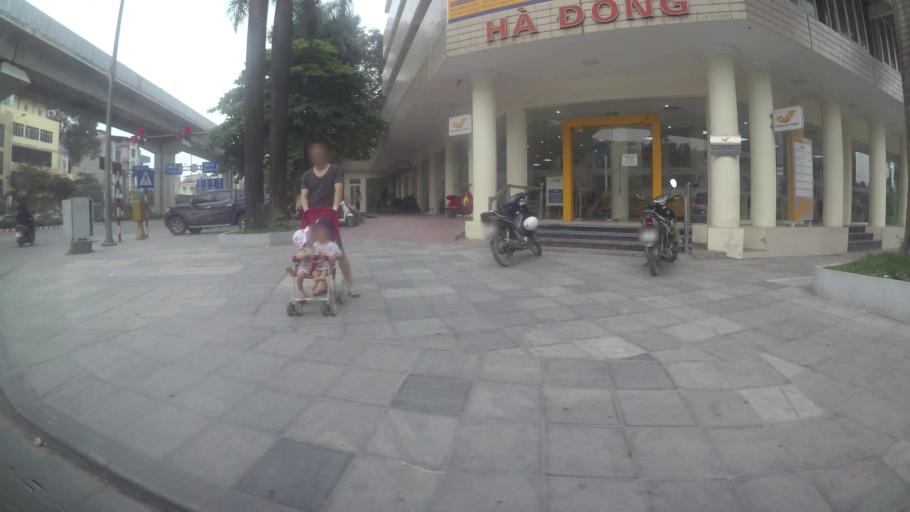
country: VN
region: Ha Noi
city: Ha Dong
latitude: 20.9734
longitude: 105.7785
